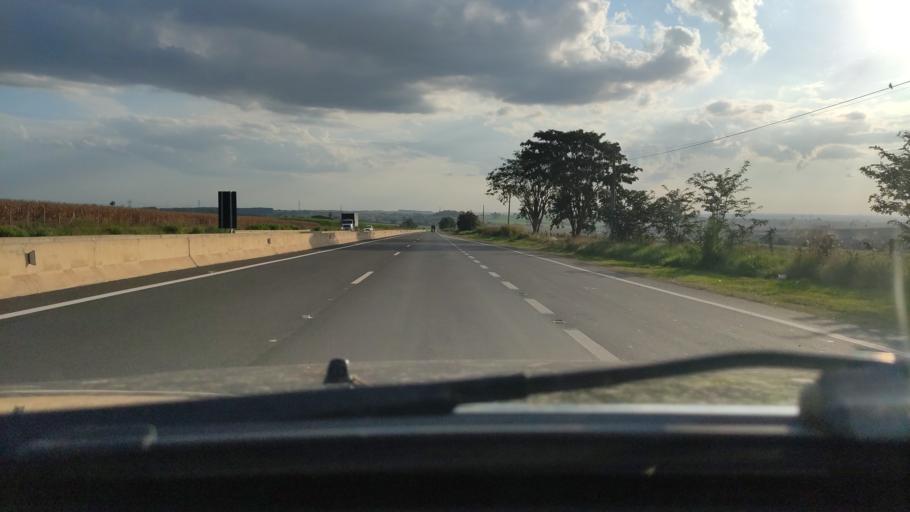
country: BR
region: Sao Paulo
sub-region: Artur Nogueira
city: Artur Nogueira
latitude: -22.4708
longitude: -47.1188
